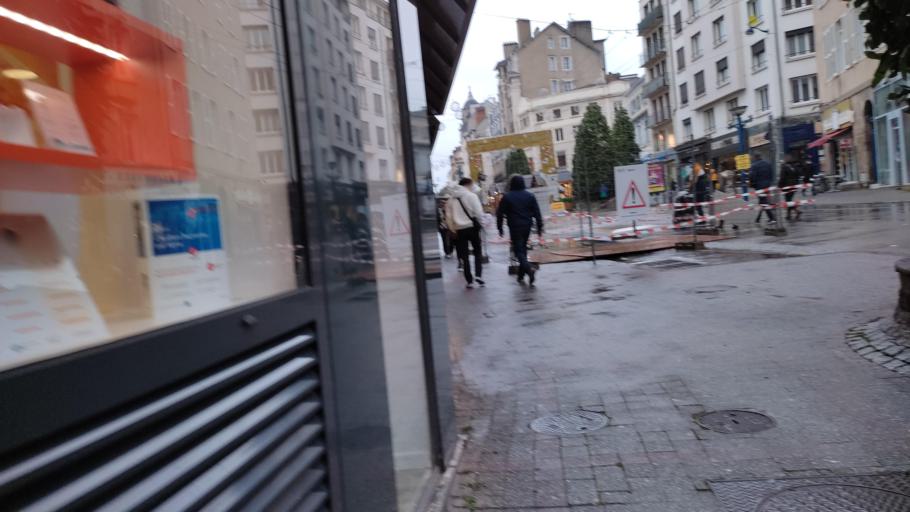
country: FR
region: Limousin
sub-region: Departement de la Haute-Vienne
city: Limoges
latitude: 45.8318
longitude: 1.2586
